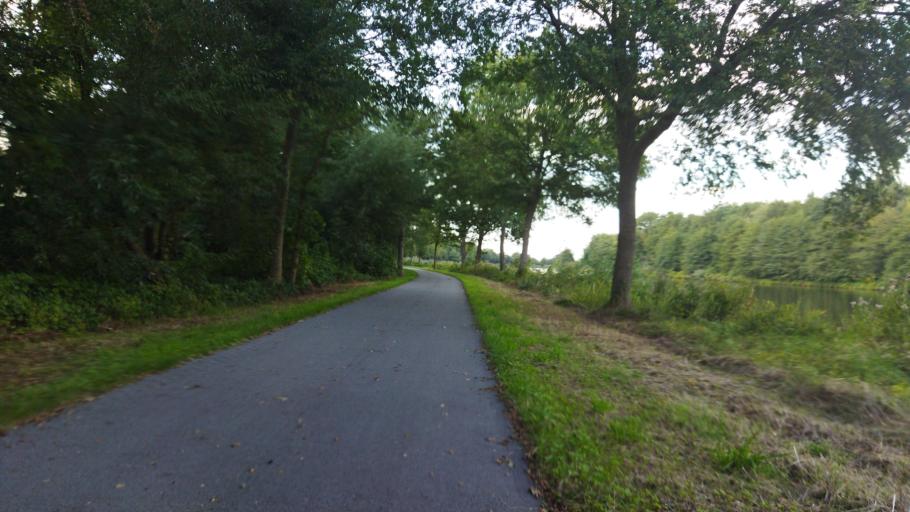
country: DE
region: Lower Saxony
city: Dersum
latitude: 52.9690
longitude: 7.3008
